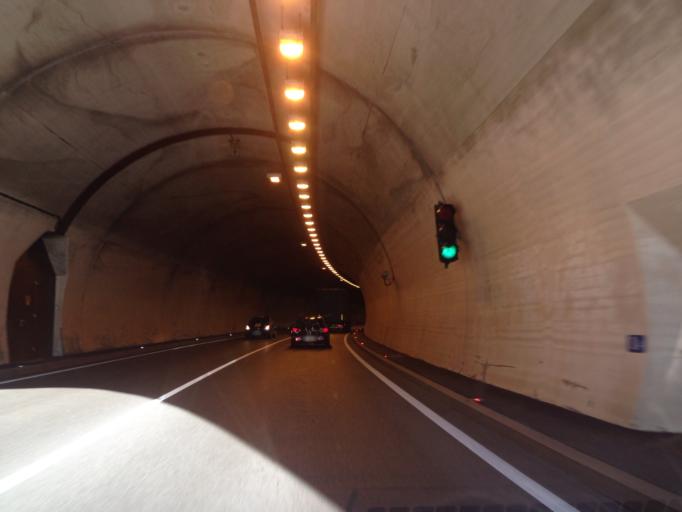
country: AT
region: Tyrol
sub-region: Politischer Bezirk Imst
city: Nassereith
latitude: 47.3064
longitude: 10.8384
